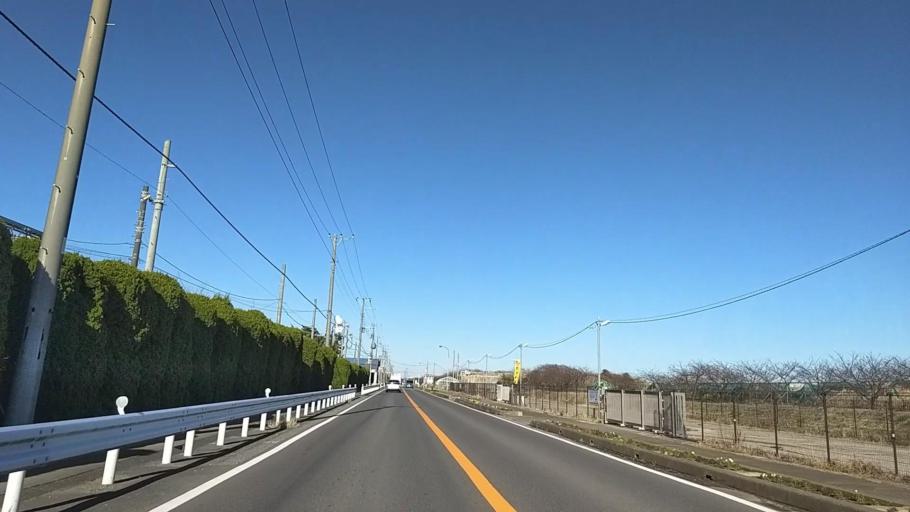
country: JP
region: Chiba
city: Togane
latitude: 35.4594
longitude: 140.4069
